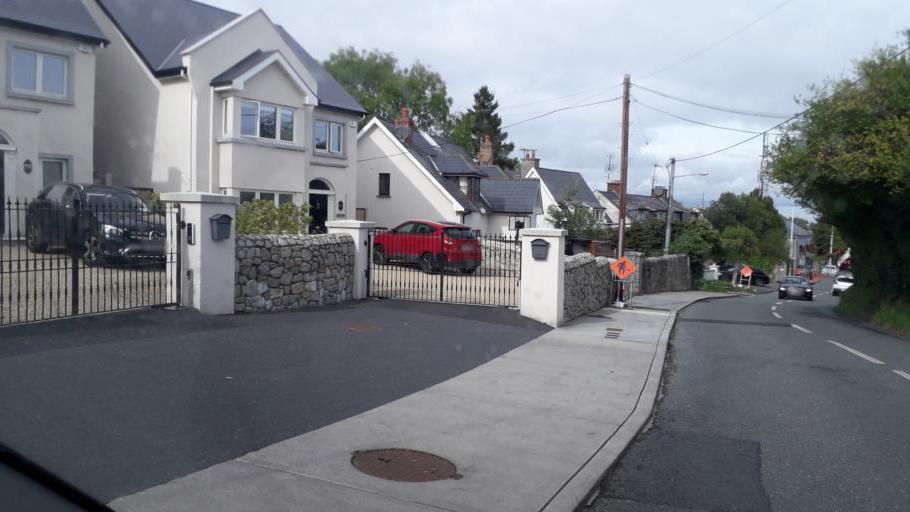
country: IE
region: Leinster
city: Sandyford
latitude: 53.2518
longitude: -6.2144
